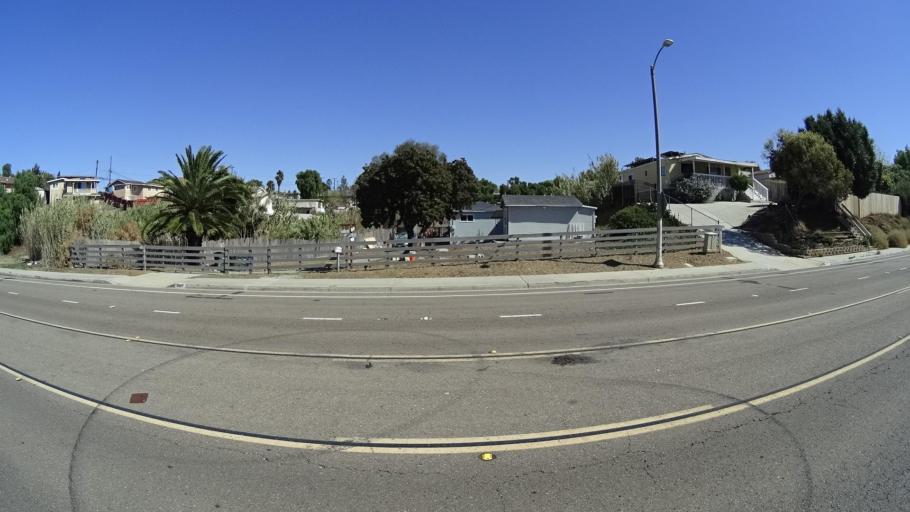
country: US
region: California
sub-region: San Diego County
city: National City
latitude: 32.6678
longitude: -117.0766
